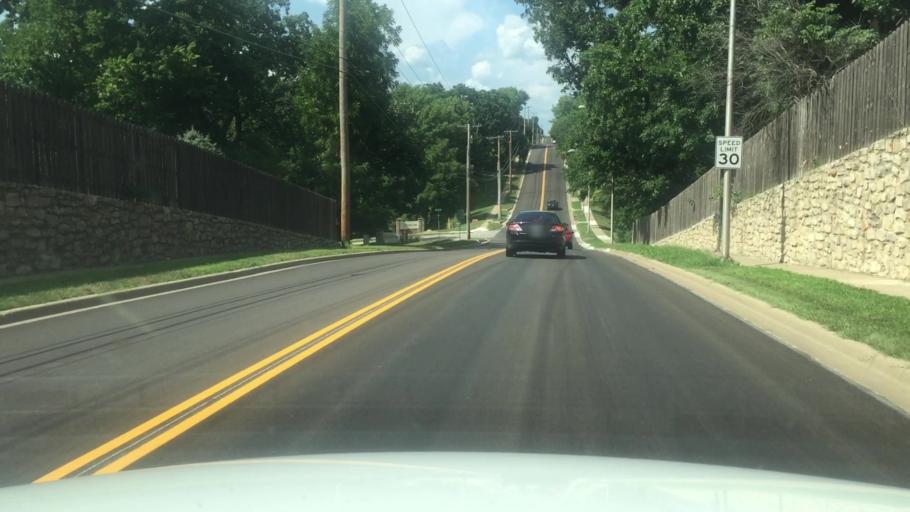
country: US
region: Kansas
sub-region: Johnson County
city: Lenexa
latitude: 38.9806
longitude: -94.7423
